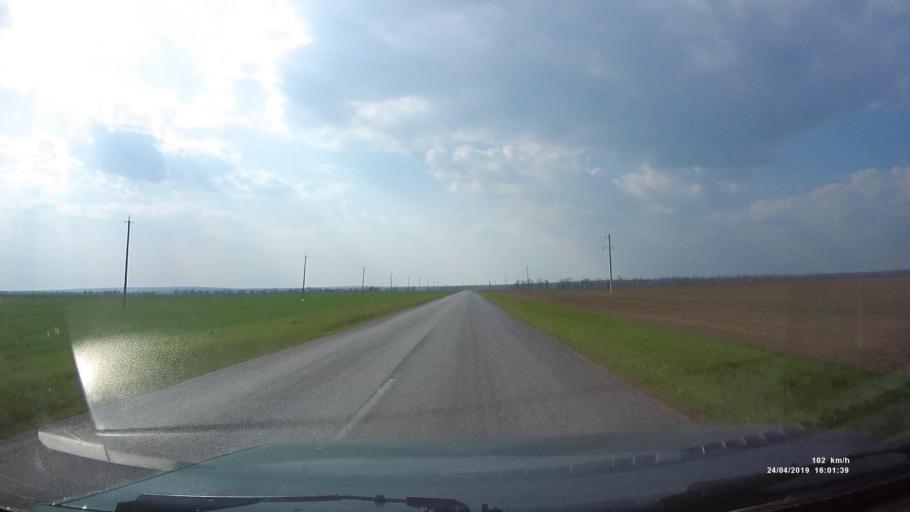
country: RU
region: Rostov
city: Sovetskoye
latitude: 46.6436
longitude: 42.4325
